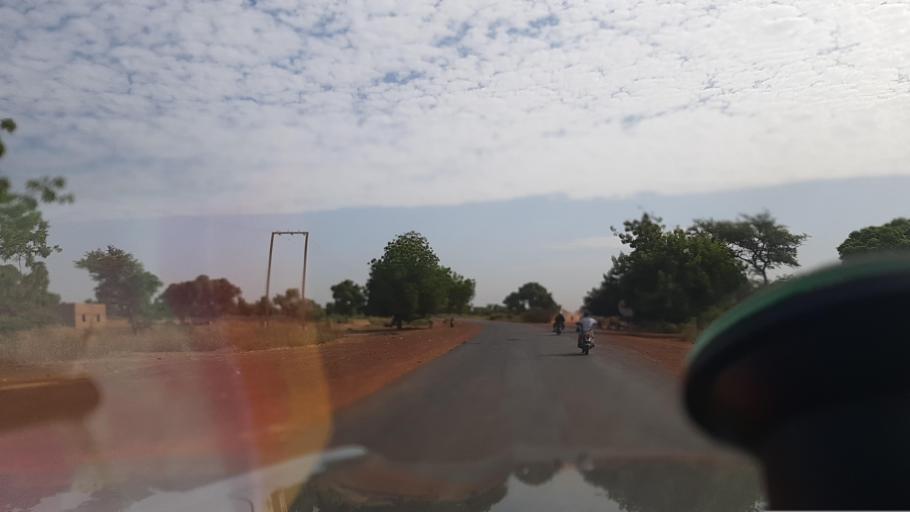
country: ML
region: Segou
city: Segou
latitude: 13.4995
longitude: -6.1539
